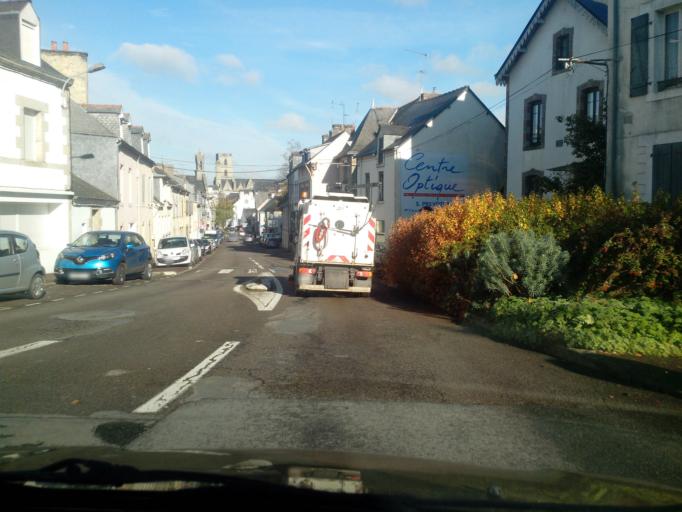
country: FR
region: Brittany
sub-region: Departement du Morbihan
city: Ploermel
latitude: 47.9284
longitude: -2.3992
